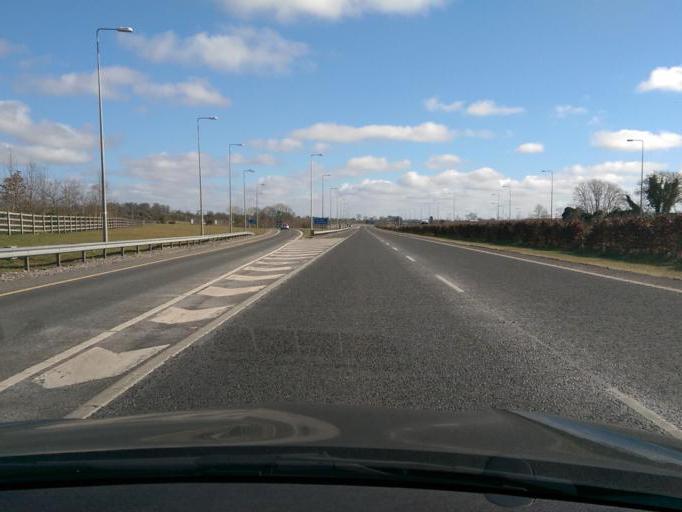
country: IE
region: Leinster
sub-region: An Mhi
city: Enfield
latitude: 53.4119
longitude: -6.8833
